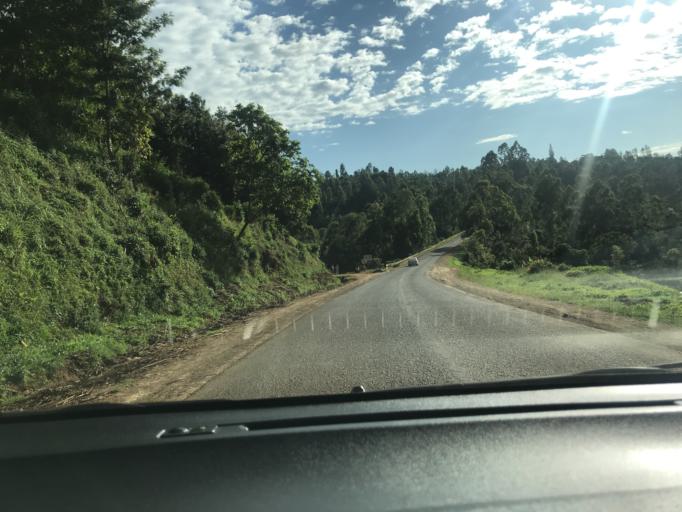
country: KE
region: Kirinyaga
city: Keruguya
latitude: -0.4876
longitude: 37.2113
